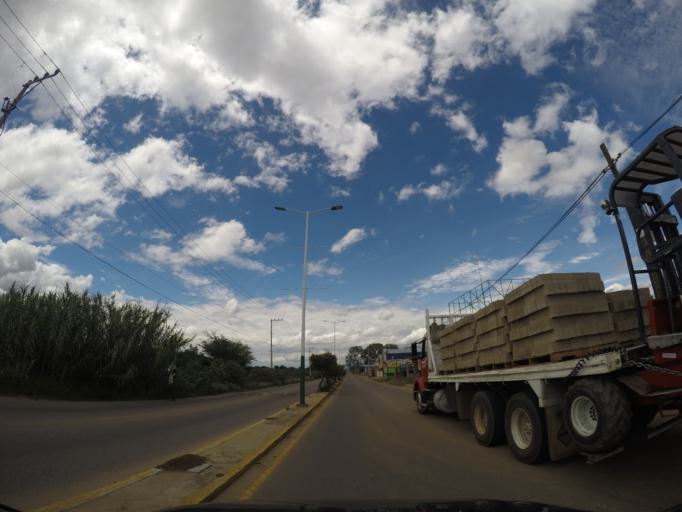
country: MX
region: Oaxaca
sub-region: Santa Cruz Xoxocotlan
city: San Isidro Monjas
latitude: 17.0034
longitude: -96.7388
